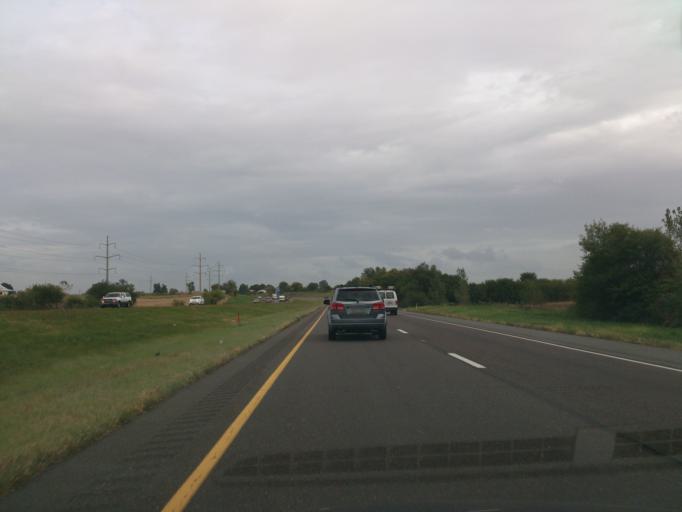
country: US
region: Pennsylvania
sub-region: Lancaster County
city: Akron
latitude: 40.1499
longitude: -76.1726
